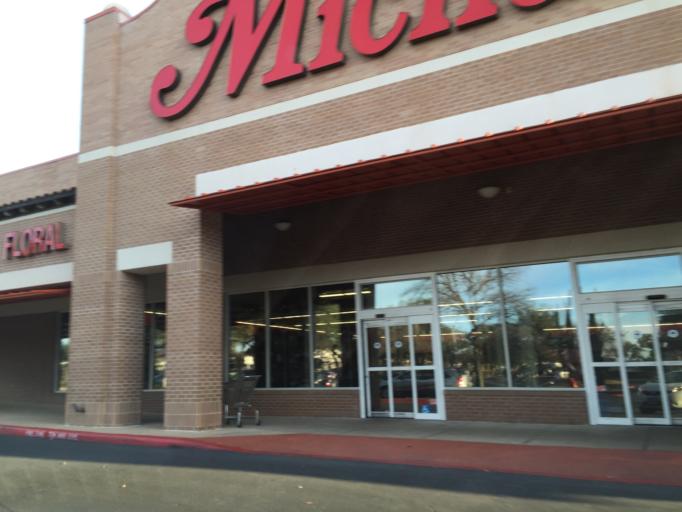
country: US
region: Texas
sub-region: Williamson County
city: Jollyville
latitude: 30.3944
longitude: -97.7442
